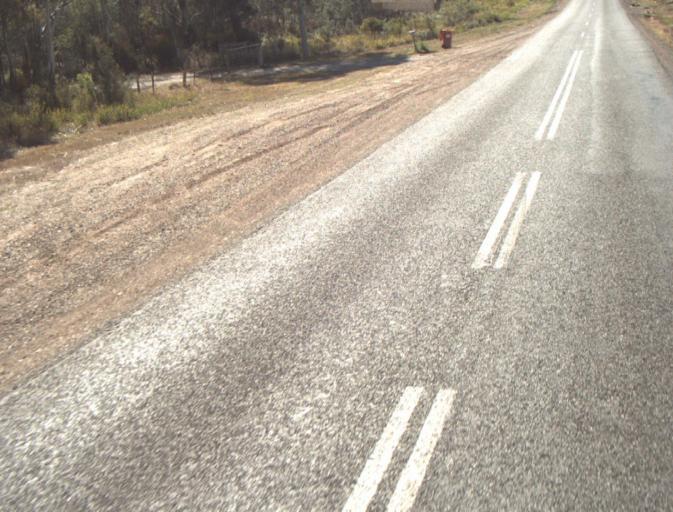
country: AU
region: Tasmania
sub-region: Launceston
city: Mayfield
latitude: -41.3134
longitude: 147.1348
